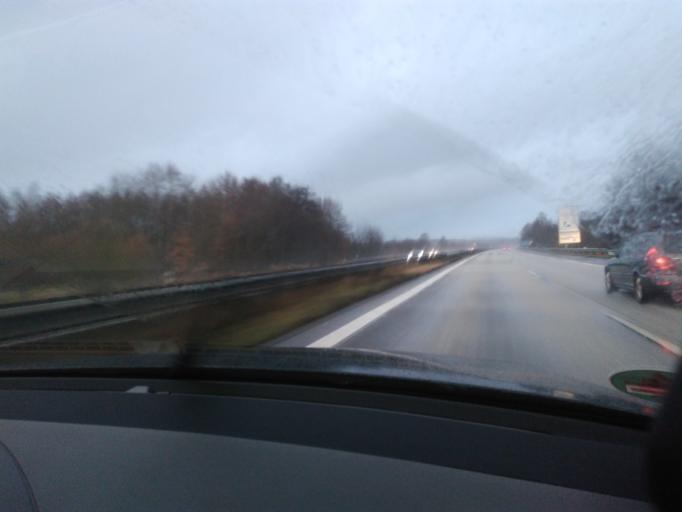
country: DE
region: Schleswig-Holstein
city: Bimohlen
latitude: 53.9111
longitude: 9.9368
